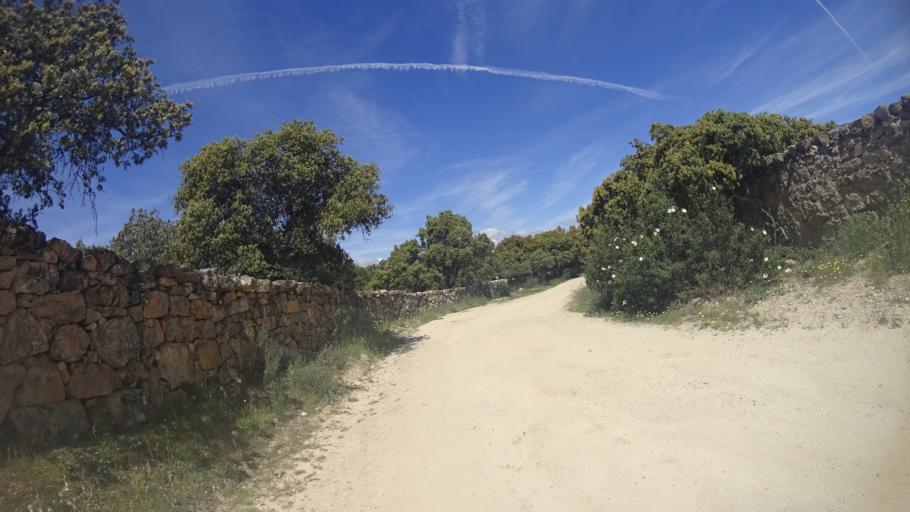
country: ES
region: Madrid
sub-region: Provincia de Madrid
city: Galapagar
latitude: 40.5574
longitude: -3.9844
